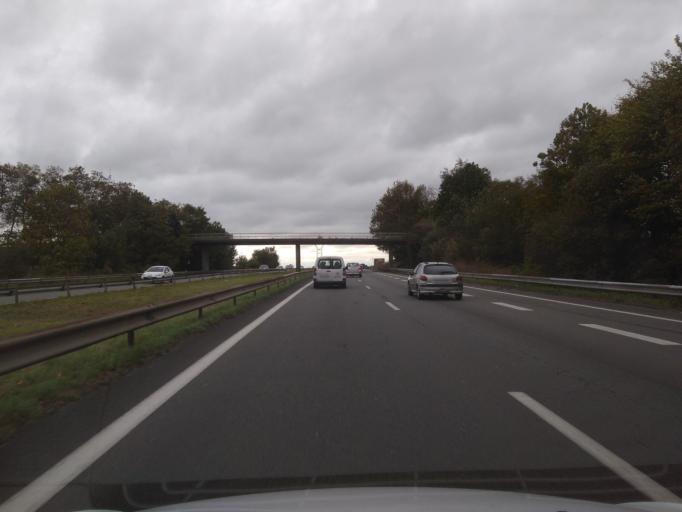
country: FR
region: Nord-Pas-de-Calais
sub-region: Departement du Nord
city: Genech
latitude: 50.5128
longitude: 3.2102
